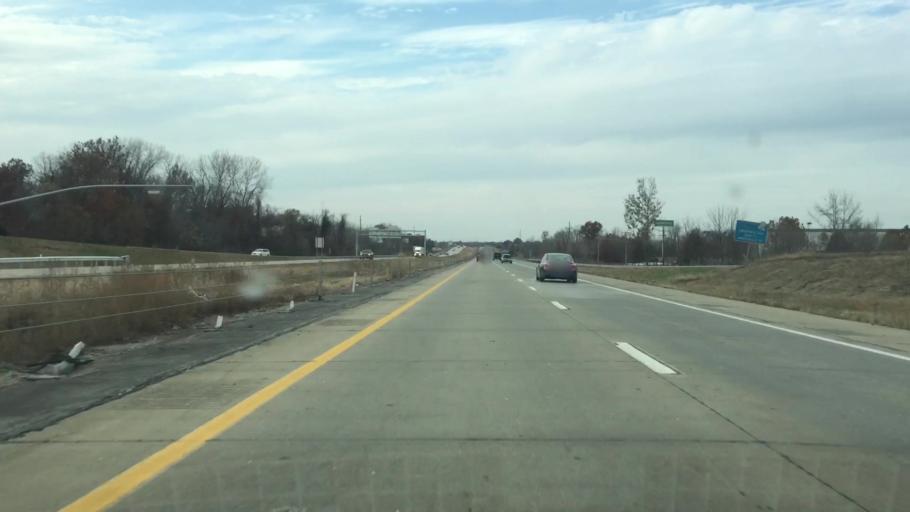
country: US
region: Missouri
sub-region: Cass County
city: Harrisonville
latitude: 38.6370
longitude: -94.3541
